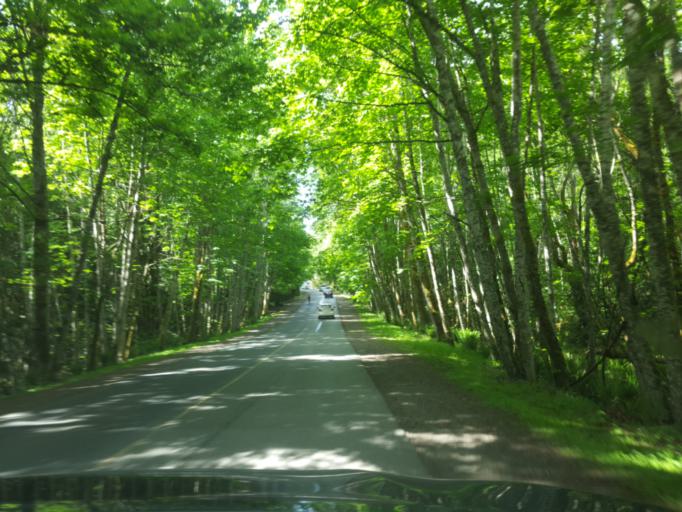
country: CA
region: British Columbia
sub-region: Regional District of Nanaimo
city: Parksville
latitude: 49.3165
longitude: -124.2732
